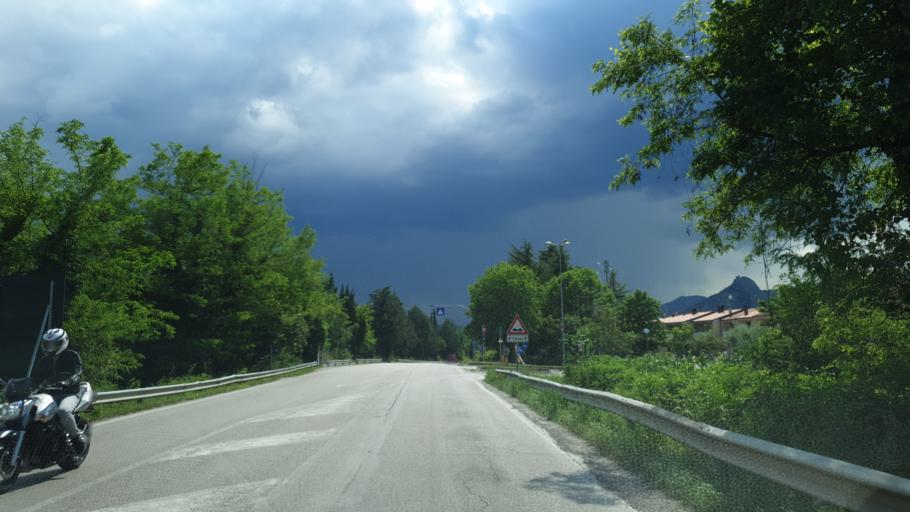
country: IT
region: Emilia-Romagna
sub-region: Provincia di Rimini
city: Pietracuta
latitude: 43.9502
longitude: 12.3665
